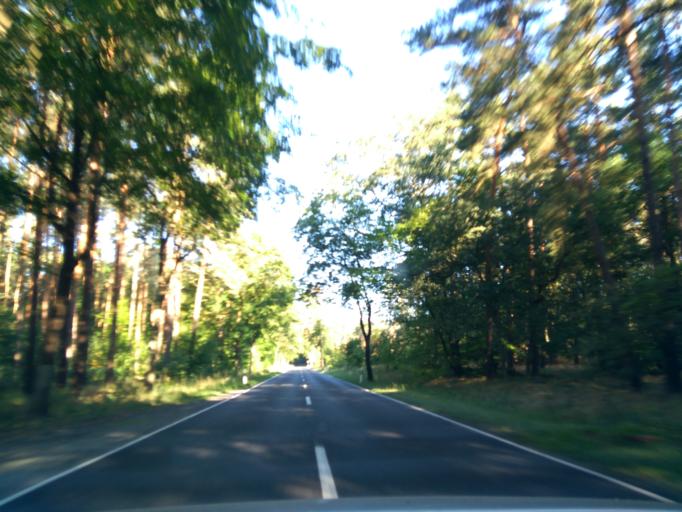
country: DE
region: Brandenburg
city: Brieselang
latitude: 52.6171
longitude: 12.9955
